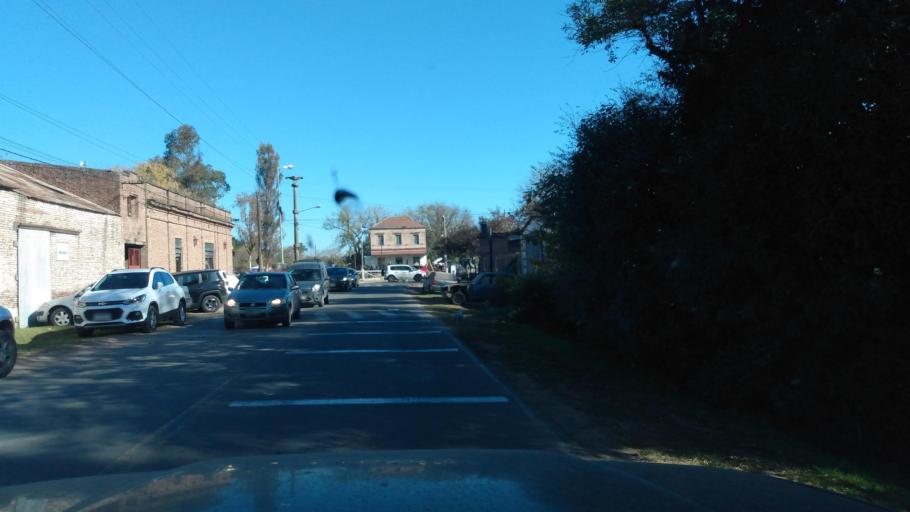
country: AR
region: Buenos Aires
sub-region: Partido de Lujan
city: Lujan
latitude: -34.4857
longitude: -59.2185
